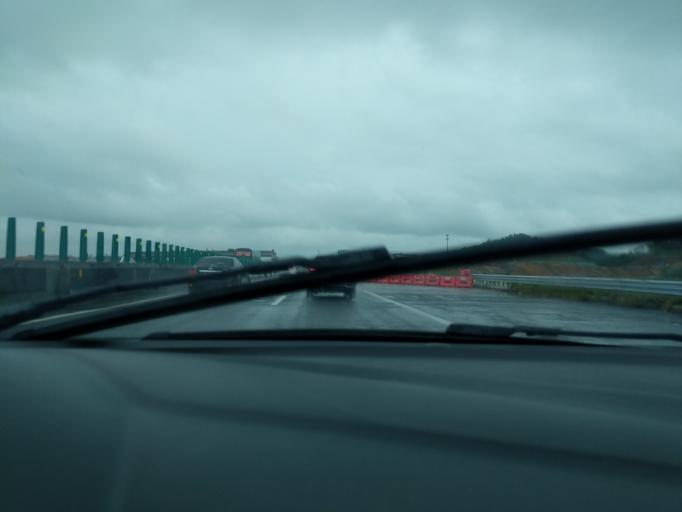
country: CN
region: Guangdong
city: Yueshan
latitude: 22.4644
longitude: 112.7079
